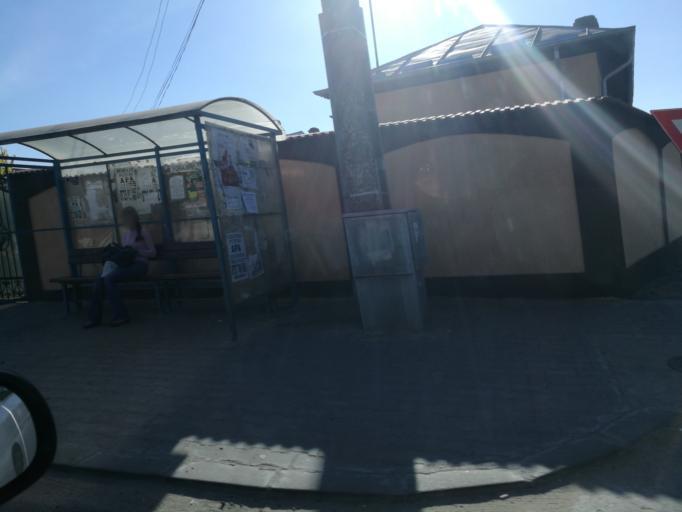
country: RO
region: Ilfov
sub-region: Comuna Dragomiresti-Vale
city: Dragomiresti-Deal
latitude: 44.4618
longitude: 25.9434
